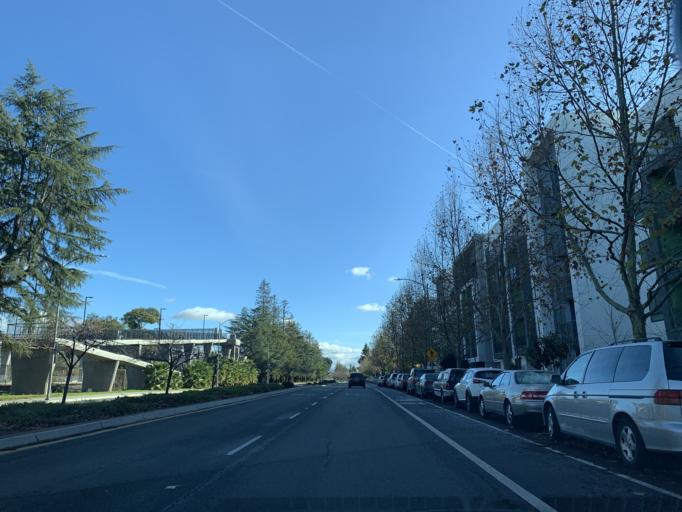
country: US
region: California
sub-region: Santa Clara County
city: Seven Trees
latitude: 37.2528
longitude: -121.7990
